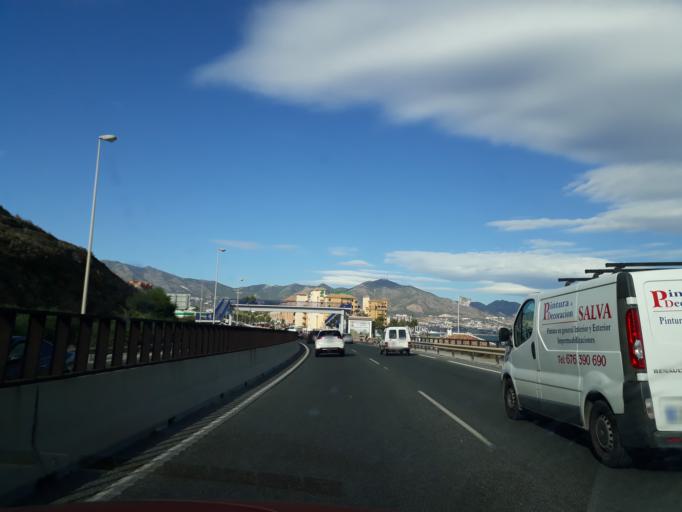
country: ES
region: Andalusia
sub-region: Provincia de Malaga
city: Fuengirola
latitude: 36.5186
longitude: -4.6303
